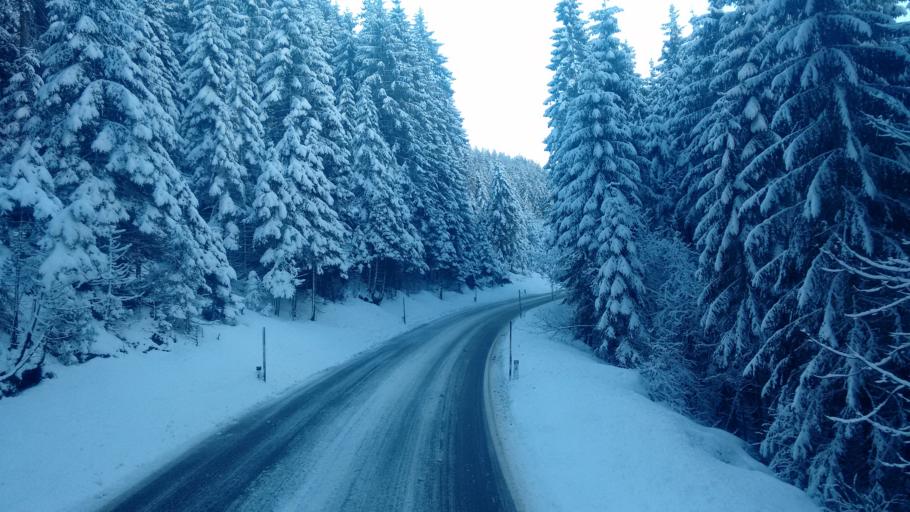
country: AT
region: Salzburg
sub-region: Politischer Bezirk Sankt Johann im Pongau
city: Radstadt
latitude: 47.3313
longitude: 13.4451
